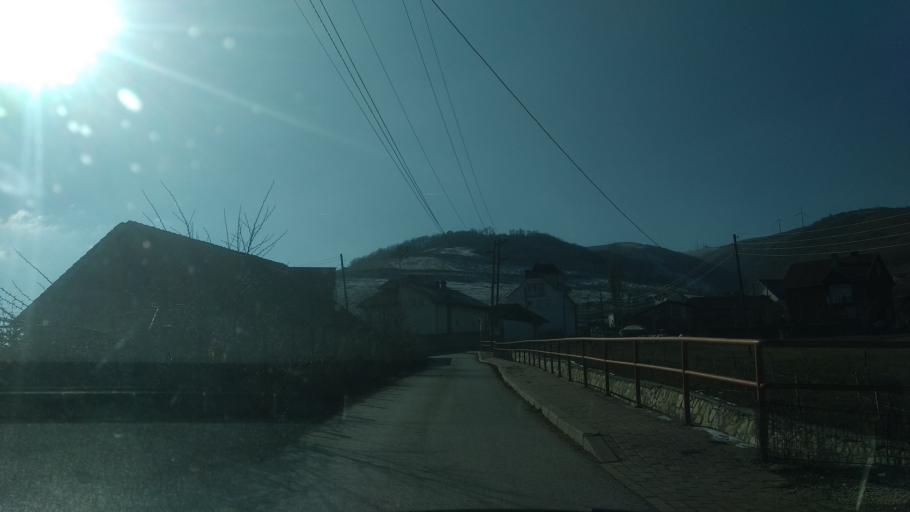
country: XK
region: Pristina
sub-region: Komuna e Gracanices
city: Glanica
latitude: 42.5848
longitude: 21.0033
